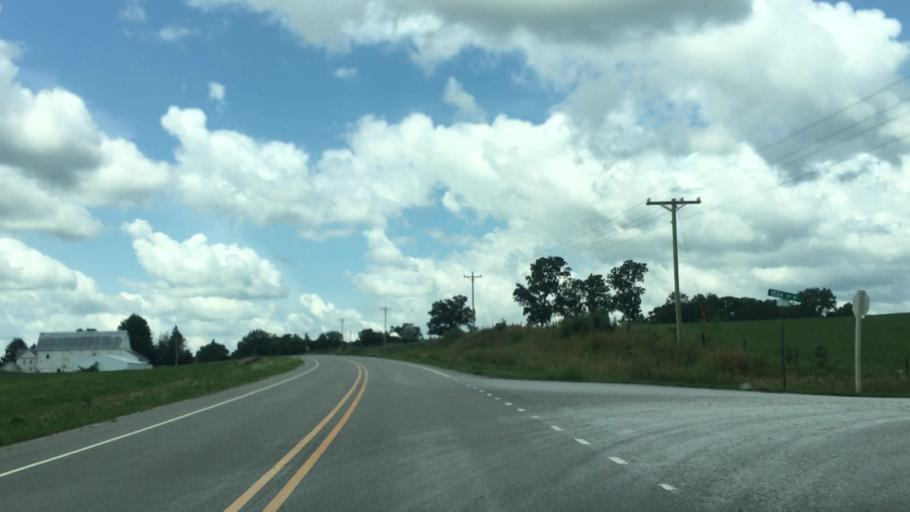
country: US
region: Iowa
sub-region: Linn County
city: Mount Vernon
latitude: 41.8427
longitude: -91.4173
